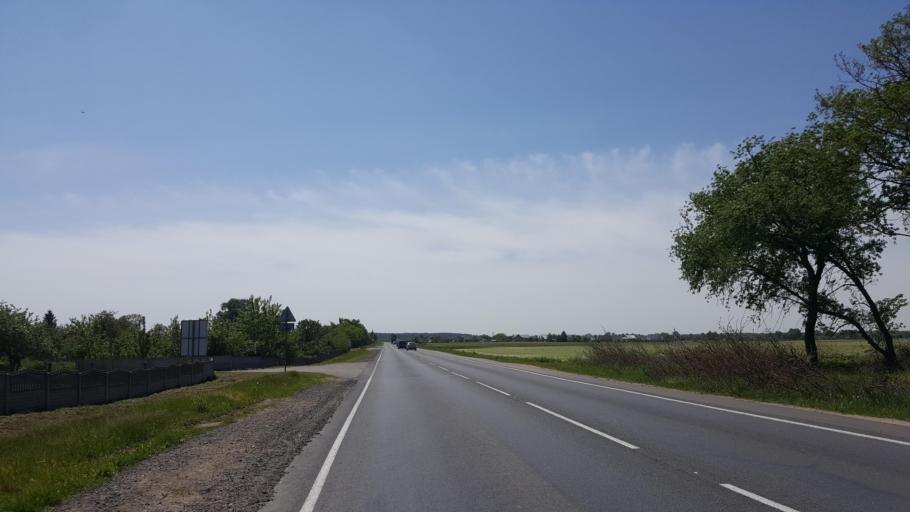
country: BY
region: Brest
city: Charnawchytsy
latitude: 52.1986
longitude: 23.7325
